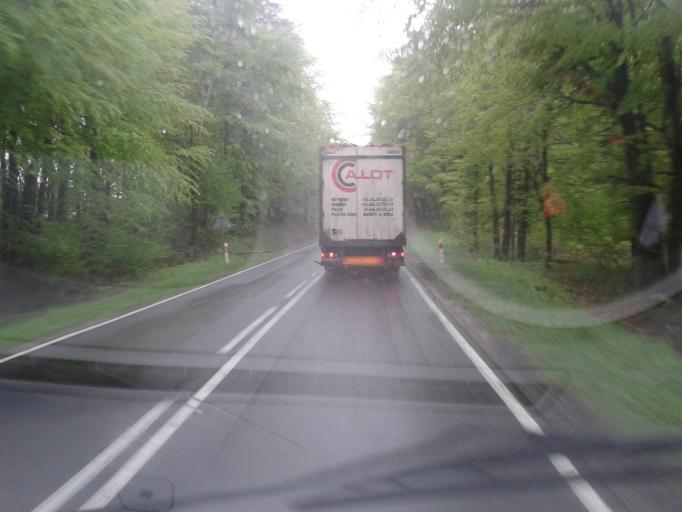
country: PL
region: Subcarpathian Voivodeship
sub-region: Powiat lubaczowski
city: Narol
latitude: 50.3309
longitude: 23.2879
